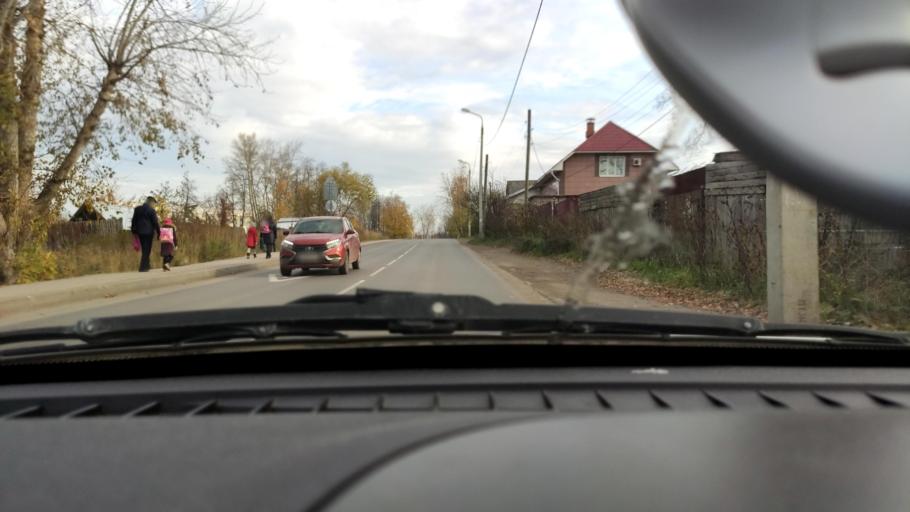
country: RU
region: Perm
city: Perm
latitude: 58.0871
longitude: 56.3988
